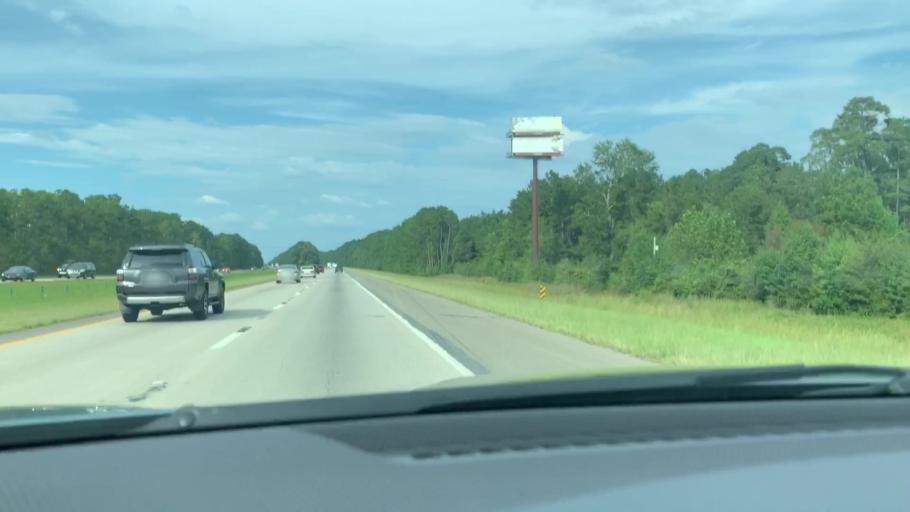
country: US
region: South Carolina
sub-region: Colleton County
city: Walterboro
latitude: 32.9580
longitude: -80.6791
